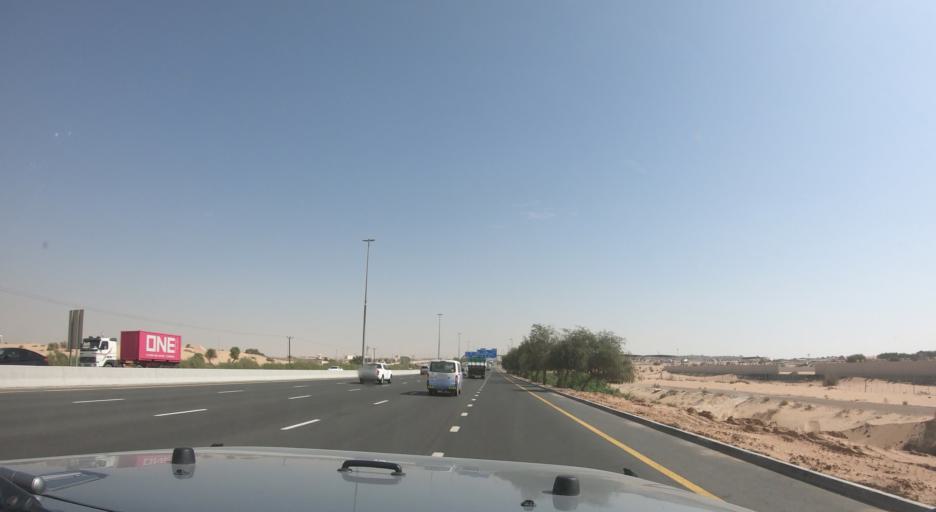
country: AE
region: Ash Shariqah
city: Sharjah
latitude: 25.1649
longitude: 55.4774
